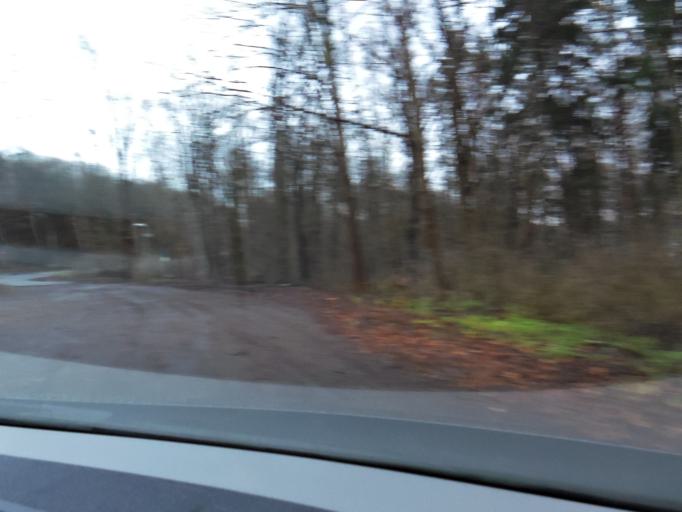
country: DE
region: Schleswig-Holstein
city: Ratzeburg
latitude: 53.7048
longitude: 10.7880
